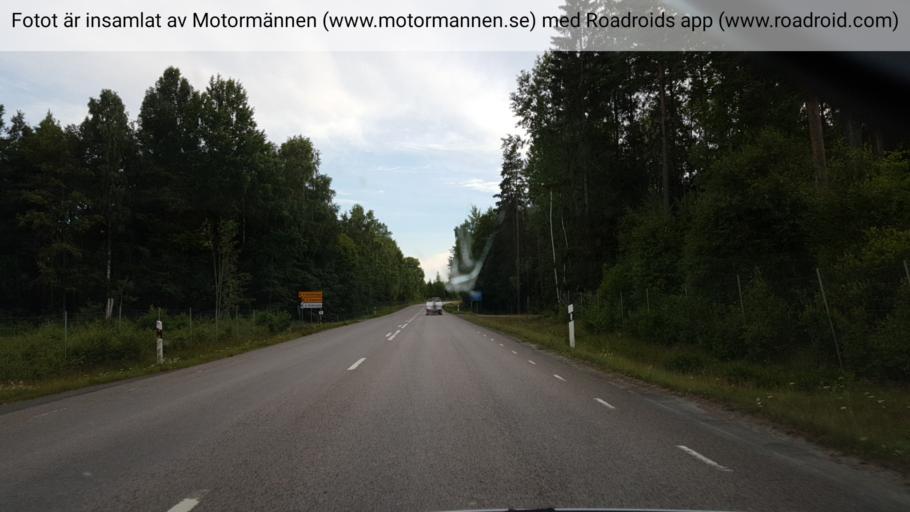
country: SE
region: Vaestra Goetaland
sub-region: Tibro Kommun
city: Tibro
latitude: 58.4375
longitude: 14.1759
